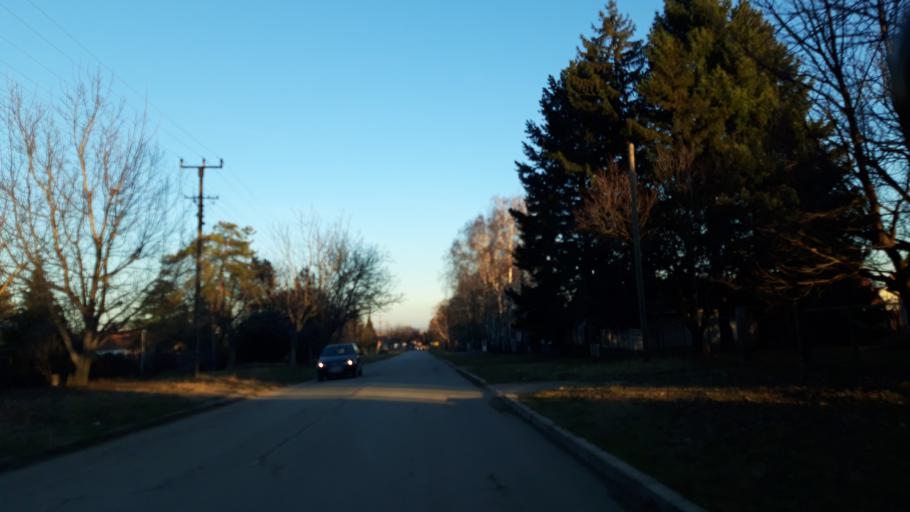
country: RS
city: Cortanovci
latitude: 45.1588
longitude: 20.0048
